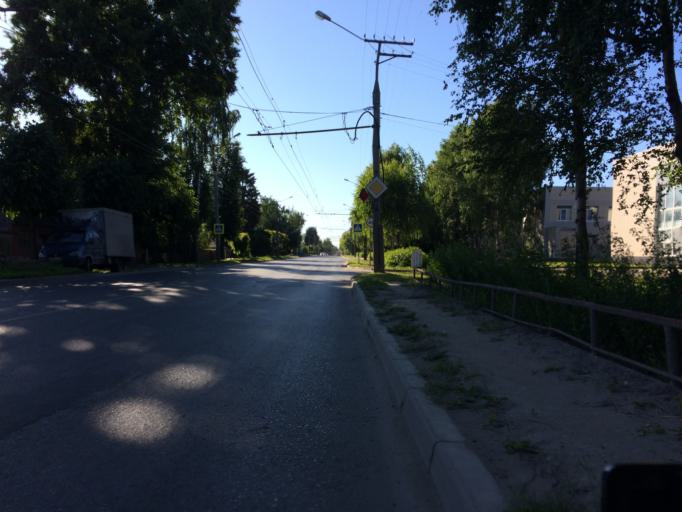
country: RU
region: Mariy-El
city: Yoshkar-Ola
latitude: 56.6529
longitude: 47.8806
